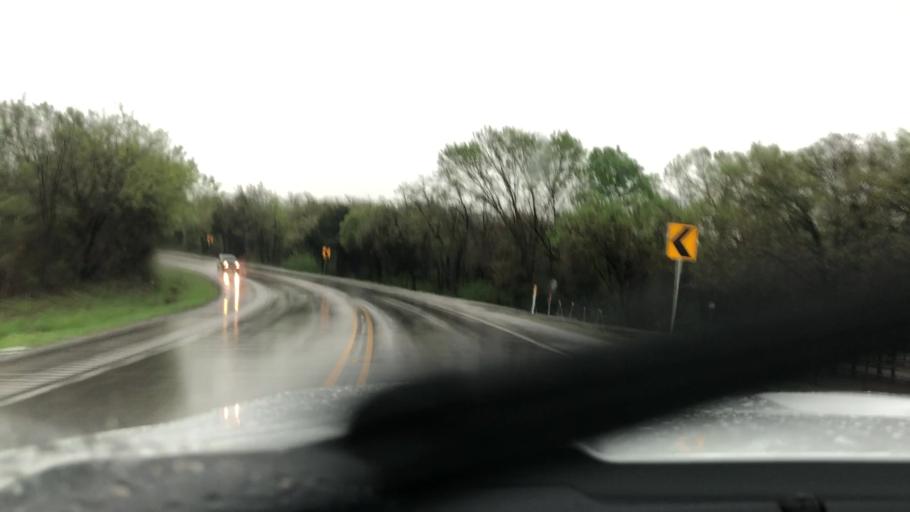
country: US
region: Texas
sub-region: Johnson County
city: Keene
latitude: 32.4529
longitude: -97.2938
